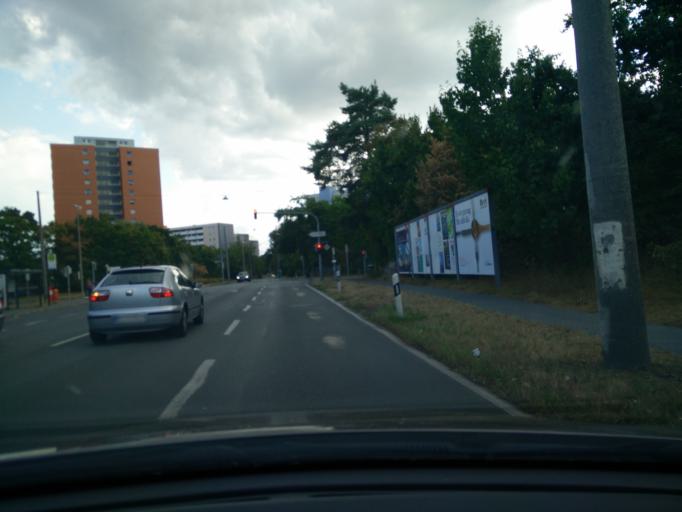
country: DE
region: Bavaria
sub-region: Regierungsbezirk Mittelfranken
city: Stein
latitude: 49.3886
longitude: 11.0328
